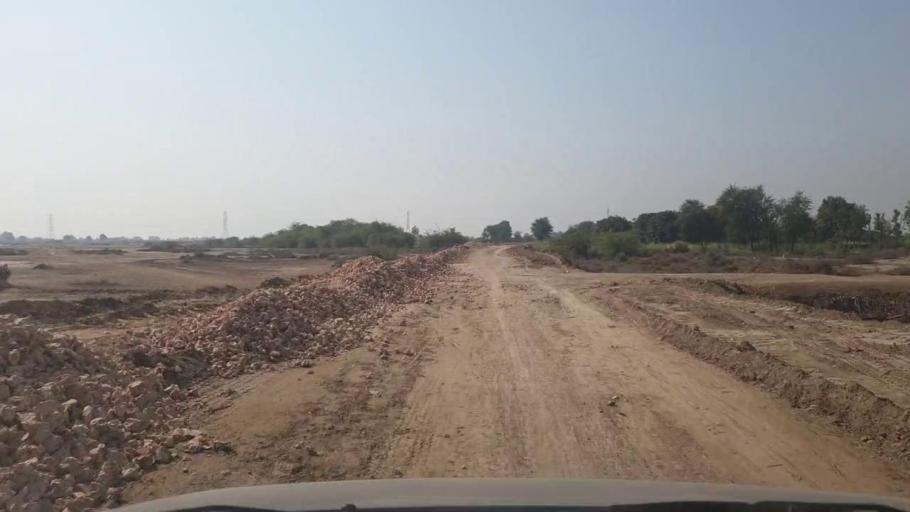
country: PK
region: Sindh
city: Mirwah Gorchani
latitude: 25.2482
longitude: 69.1093
